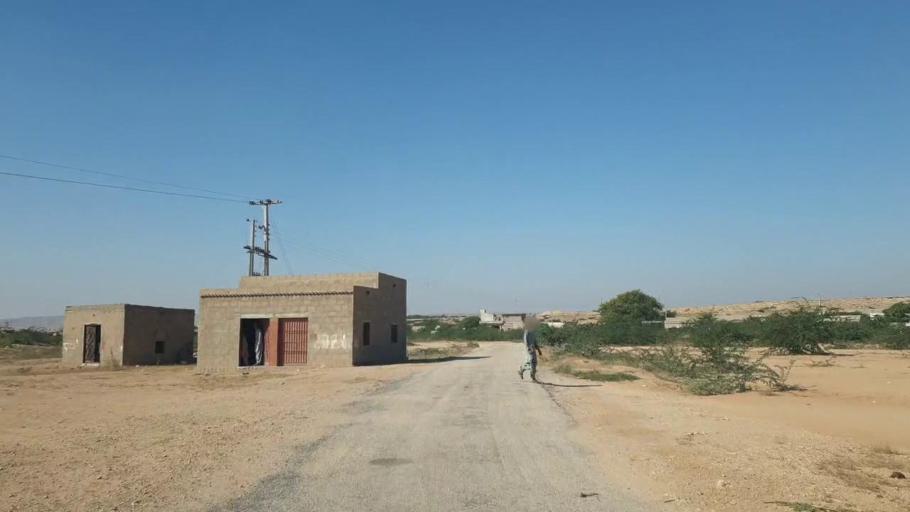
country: PK
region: Sindh
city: Gharo
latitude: 25.0895
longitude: 67.5366
